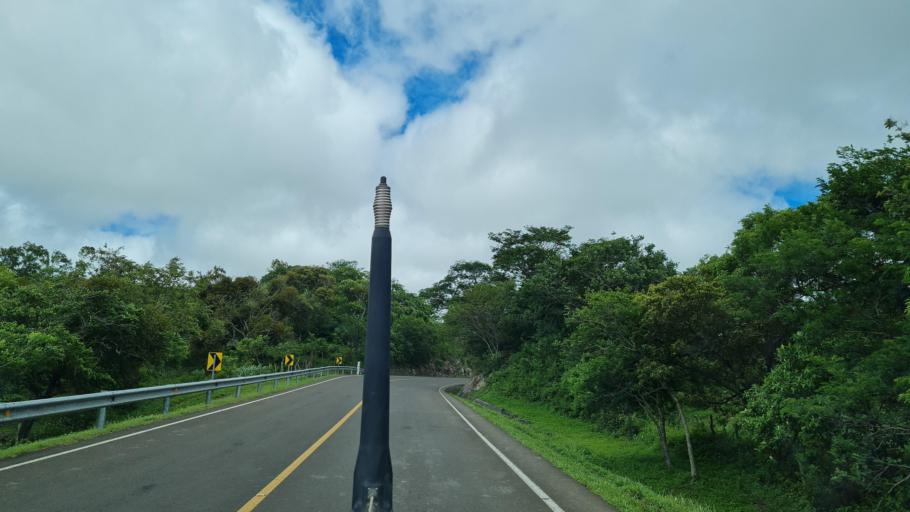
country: NI
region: Matagalpa
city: Terrabona
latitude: 12.5930
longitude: -85.9563
